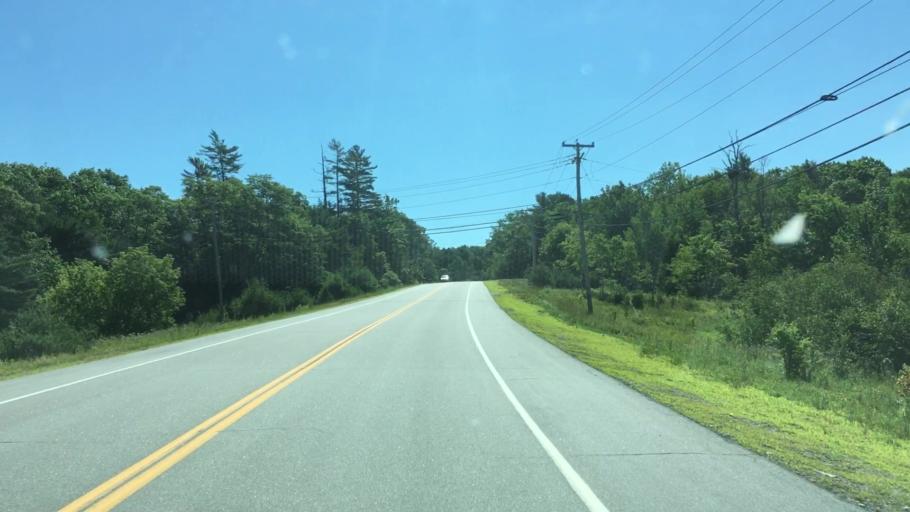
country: US
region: Maine
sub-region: Hancock County
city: Orland
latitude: 44.5584
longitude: -68.7034
